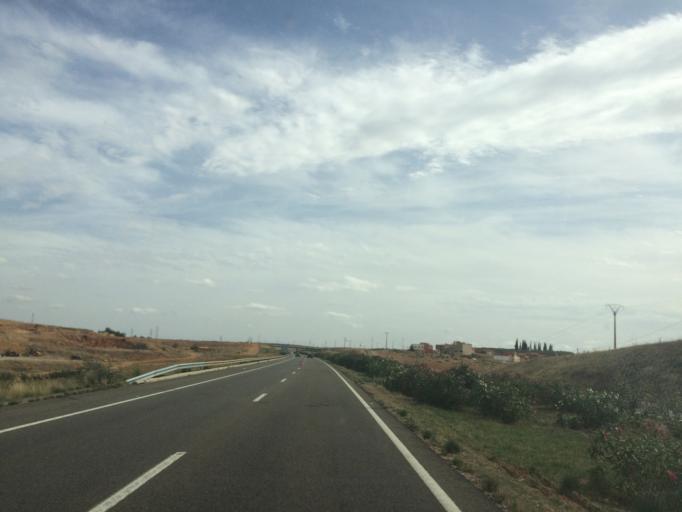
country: MA
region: Meknes-Tafilalet
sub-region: Meknes
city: Meknes
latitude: 33.8309
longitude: -5.5586
